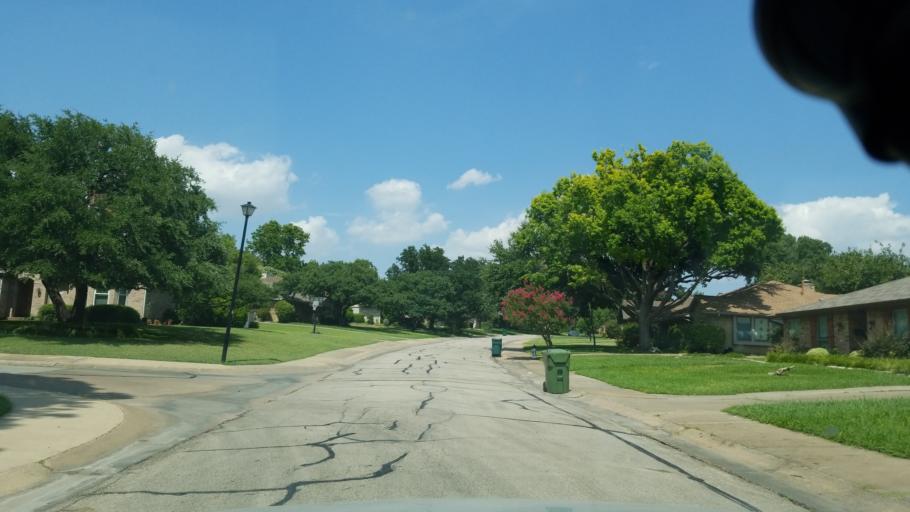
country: US
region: Texas
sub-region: Dallas County
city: Addison
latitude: 32.9655
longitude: -96.8590
